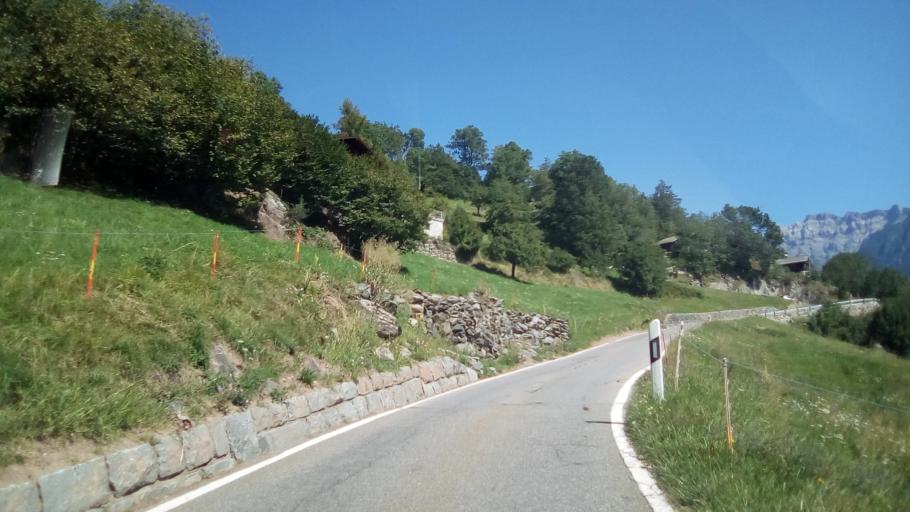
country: CH
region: Valais
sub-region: Saint-Maurice District
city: Salvan
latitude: 46.1265
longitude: 7.0235
